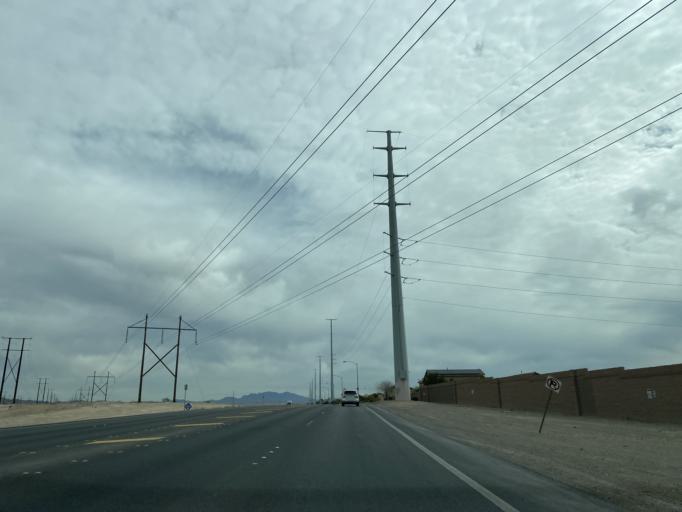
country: US
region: Nevada
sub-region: Clark County
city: Nellis Air Force Base
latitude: 36.2766
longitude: -115.0953
